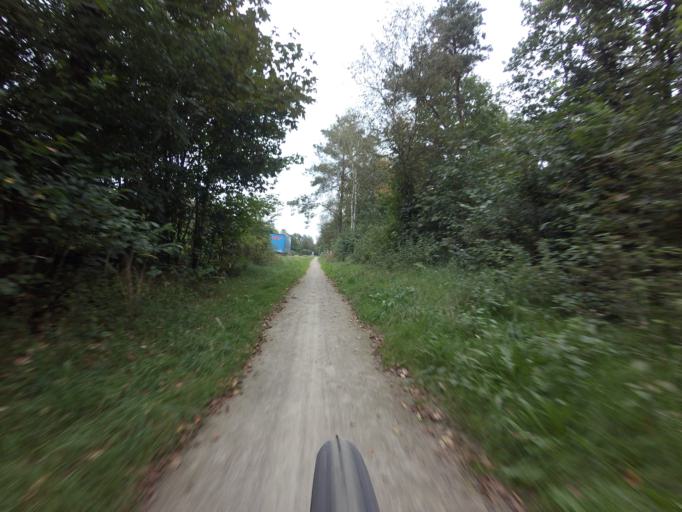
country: DK
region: South Denmark
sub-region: Billund Kommune
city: Billund
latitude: 55.8099
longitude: 9.0235
